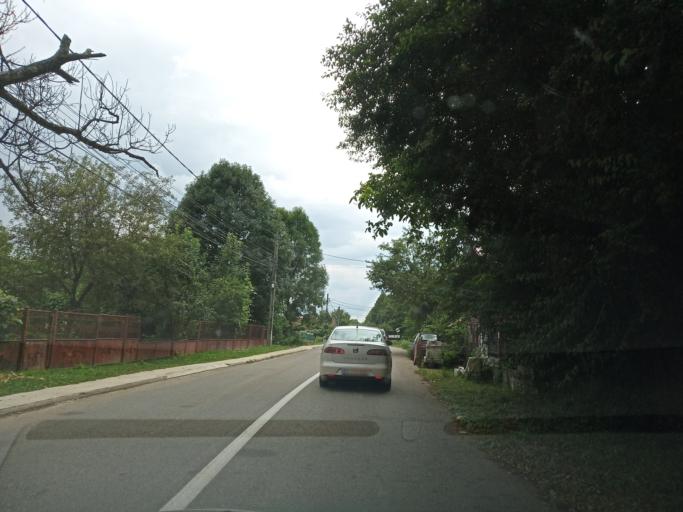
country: RO
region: Gorj
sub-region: Comuna Tismana
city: Pocruia
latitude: 45.0675
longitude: 22.9411
